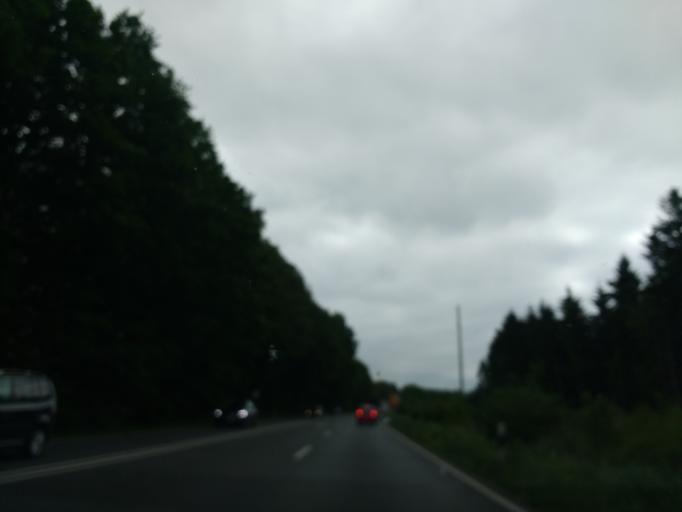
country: DE
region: Lower Saxony
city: Wunstorf
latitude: 52.4176
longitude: 9.4881
